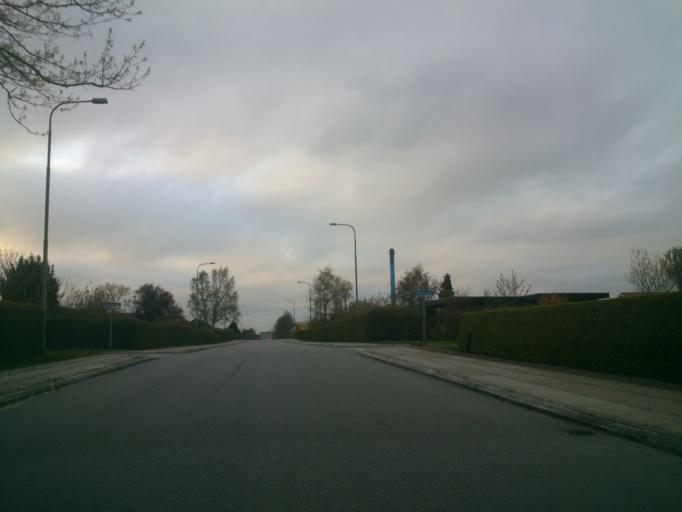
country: DK
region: South Denmark
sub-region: Fredericia Kommune
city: Fredericia
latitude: 55.5644
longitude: 9.7180
